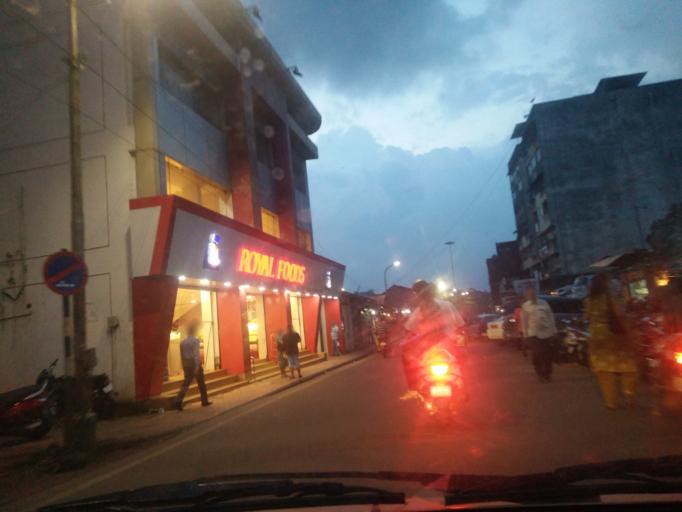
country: IN
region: Goa
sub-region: South Goa
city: Madgaon
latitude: 15.2718
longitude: 73.9605
